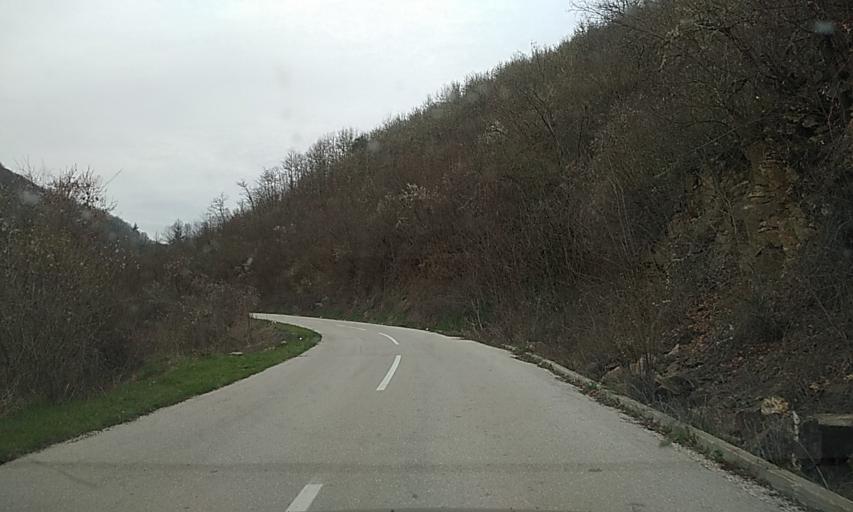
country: RS
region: Central Serbia
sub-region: Pcinjski Okrug
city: Bosilegrad
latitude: 42.4181
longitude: 22.5143
